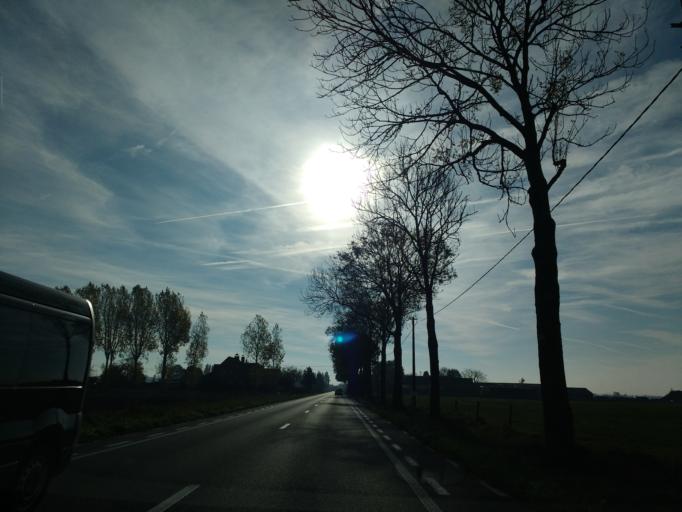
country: BE
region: Flanders
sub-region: Provincie Oost-Vlaanderen
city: Kaprijke
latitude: 51.2370
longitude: 3.6169
